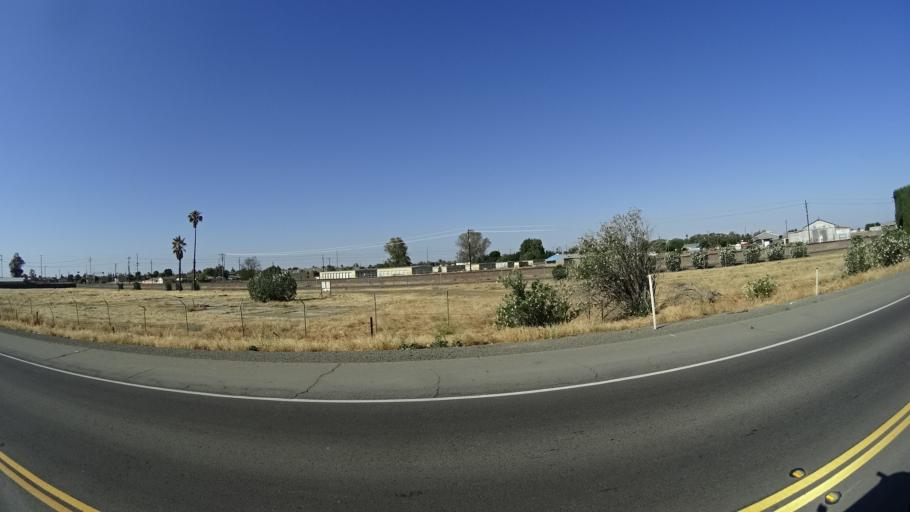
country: US
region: California
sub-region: Kings County
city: Corcoran
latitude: 36.1116
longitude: -119.5653
